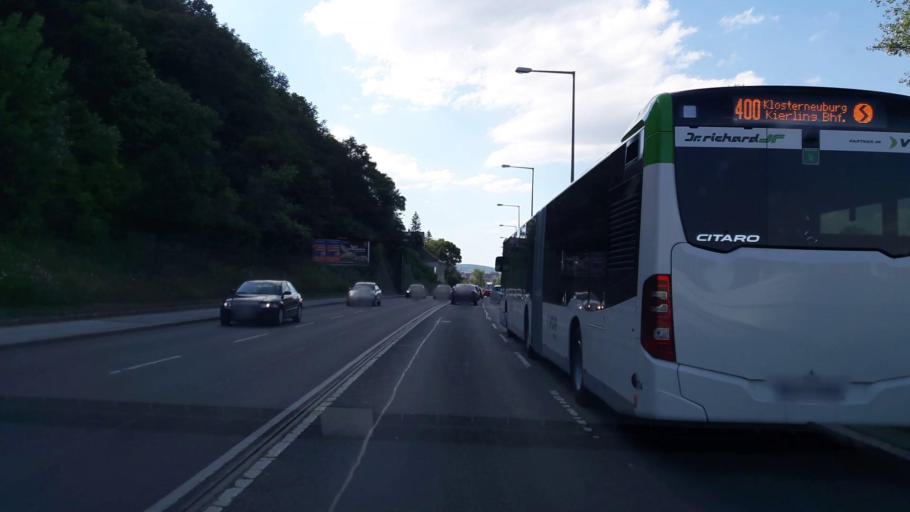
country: AT
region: Lower Austria
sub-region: Politischer Bezirk Korneuburg
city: Langenzersdorf
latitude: 48.2814
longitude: 16.3497
